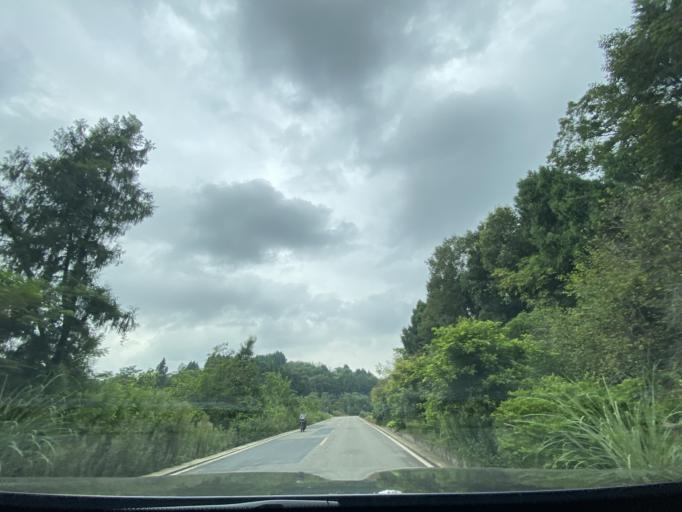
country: CN
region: Sichuan
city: Jiancheng
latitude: 30.5360
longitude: 104.5296
